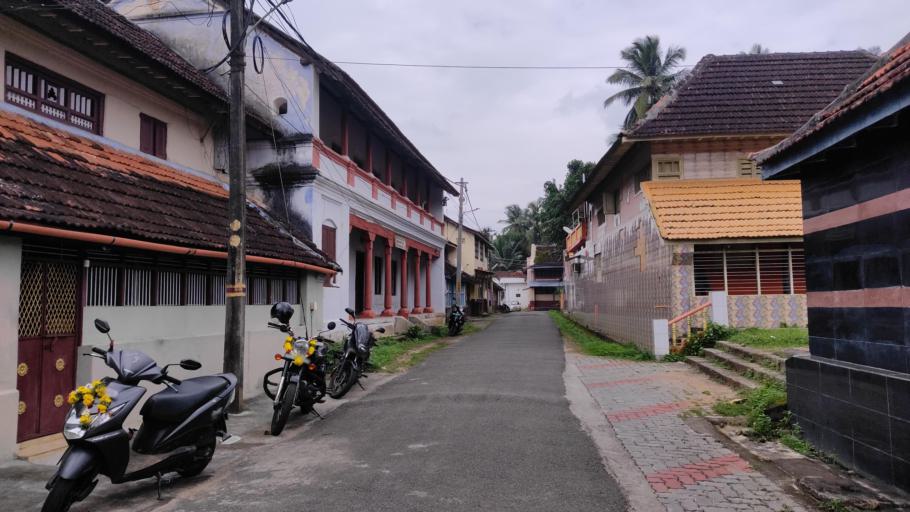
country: IN
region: Kerala
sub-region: Palakkad district
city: Chittur
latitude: 10.6929
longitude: 76.7400
